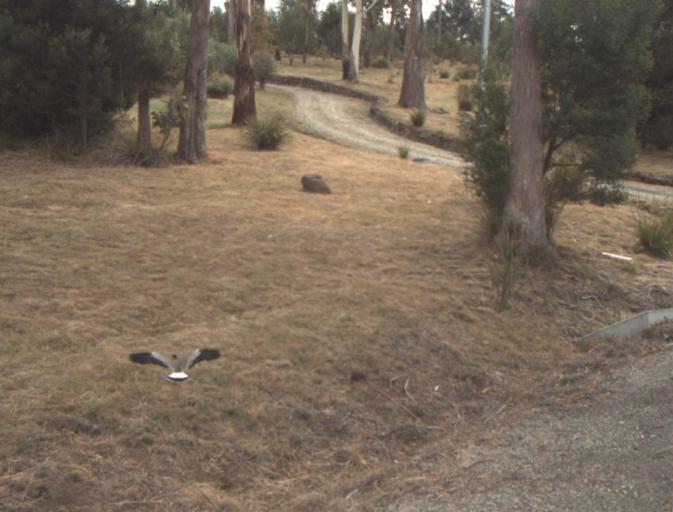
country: AU
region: Tasmania
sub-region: Launceston
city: Mayfield
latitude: -41.3041
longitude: 147.0455
